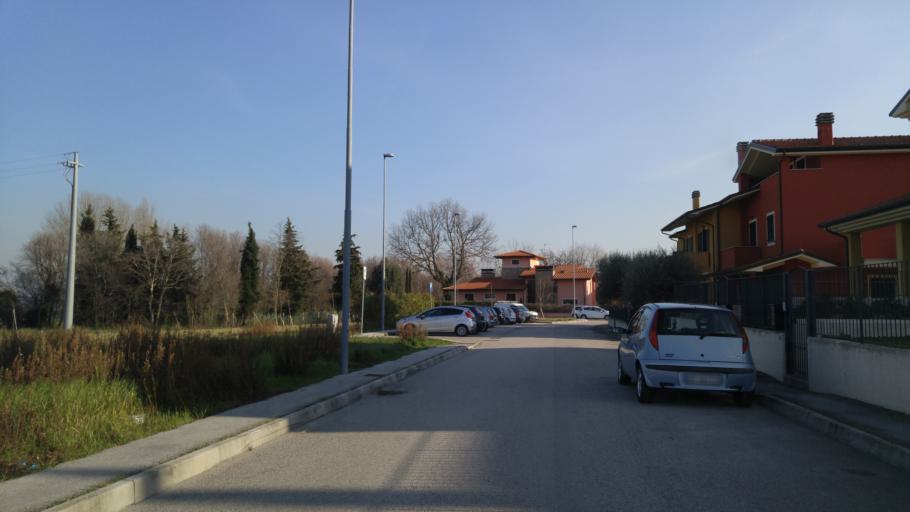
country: IT
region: The Marches
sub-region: Provincia di Pesaro e Urbino
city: Calcinelli
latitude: 43.7580
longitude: 12.9175
